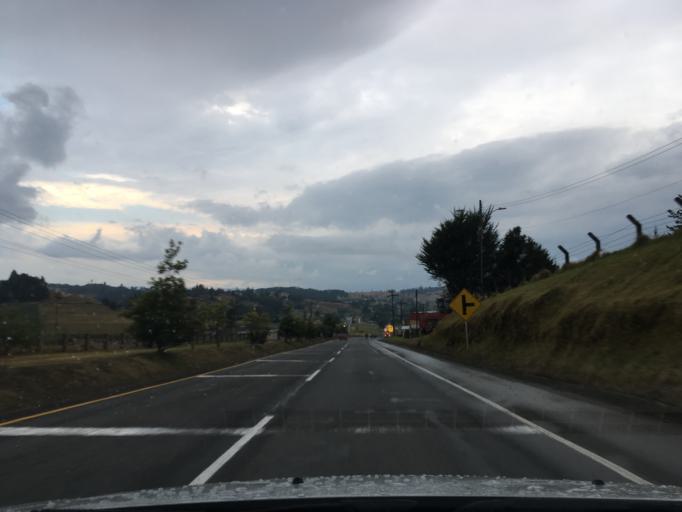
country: CO
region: Cundinamarca
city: Choconta
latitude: 5.1167
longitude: -73.6977
